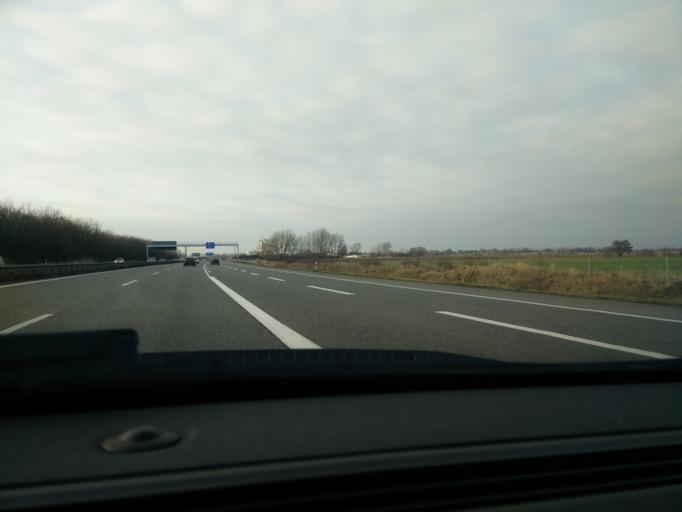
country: DE
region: Saxony
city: Borsdorf
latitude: 51.3123
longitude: 12.5420
